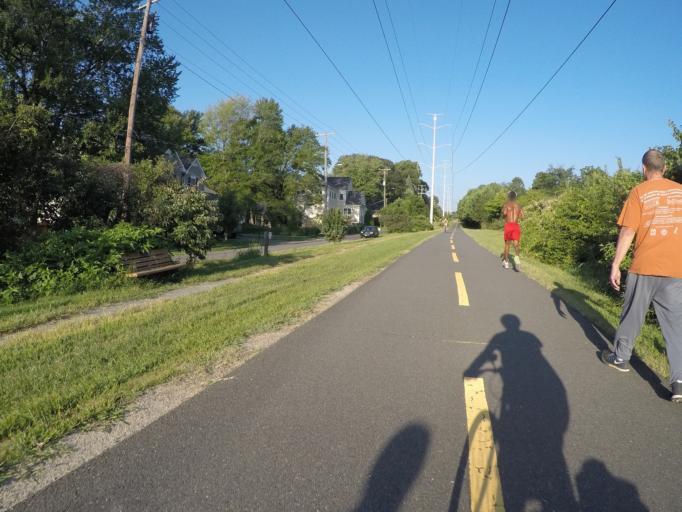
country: US
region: Virginia
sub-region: Fairfax County
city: Idylwood
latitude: 38.8917
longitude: -77.1909
